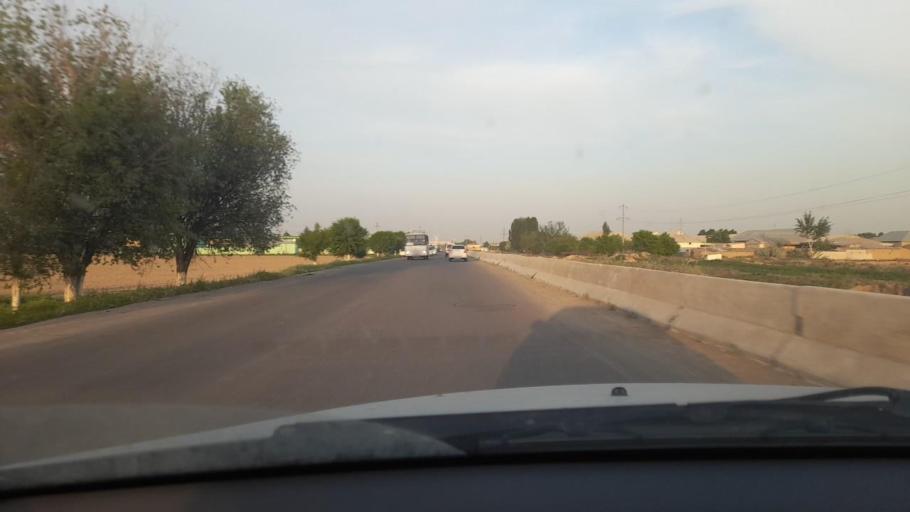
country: UZ
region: Sirdaryo
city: Guliston
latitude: 40.5076
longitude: 68.7435
